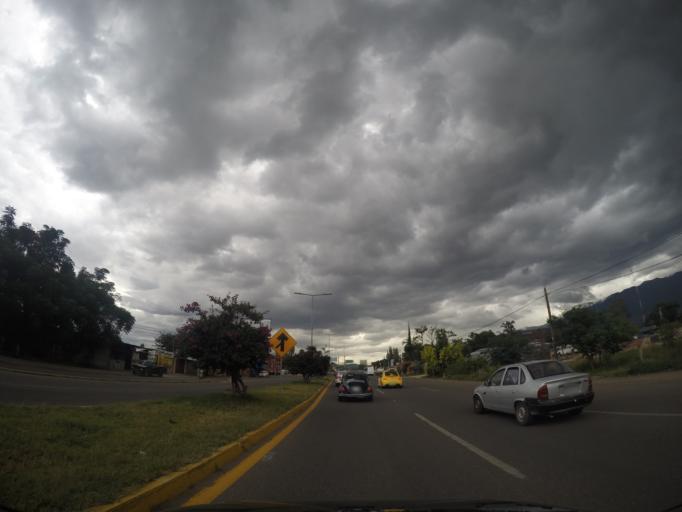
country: MX
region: Oaxaca
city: Tlalixtac de Cabrera
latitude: 17.0576
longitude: -96.6573
